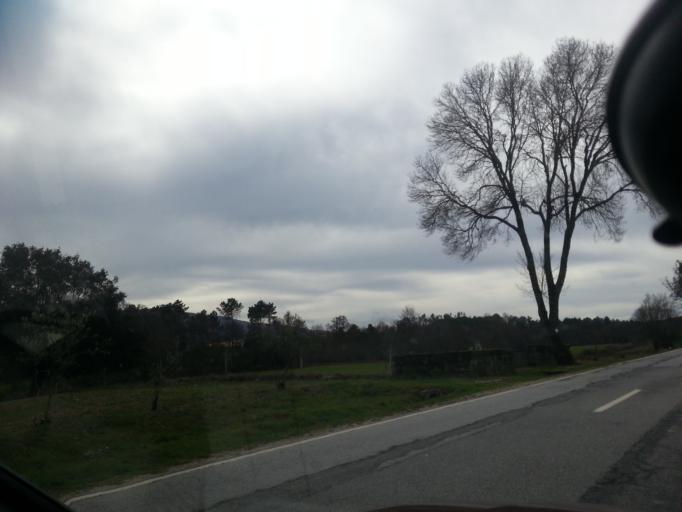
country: PT
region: Guarda
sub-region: Seia
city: Seia
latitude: 40.4563
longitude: -7.6977
